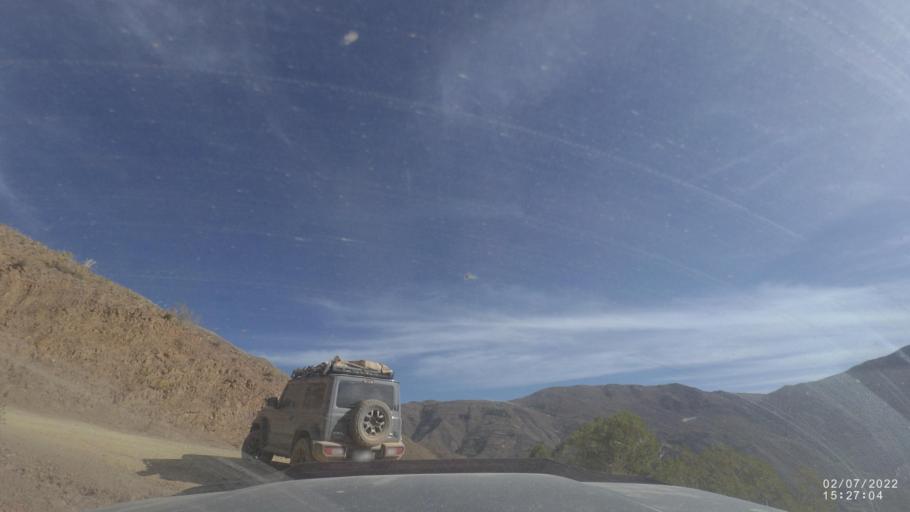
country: BO
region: Cochabamba
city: Irpa Irpa
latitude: -17.8784
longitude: -66.4153
